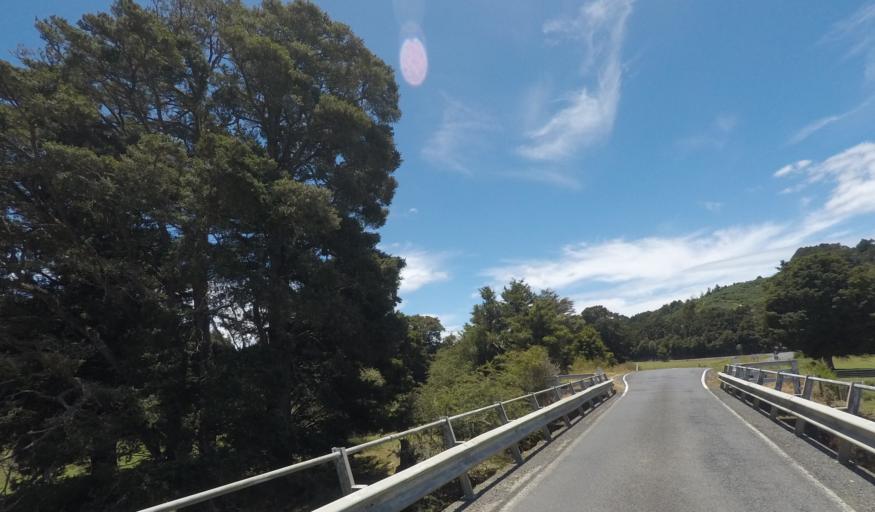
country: NZ
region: Northland
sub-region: Whangarei
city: Whangarei
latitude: -35.5421
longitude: 174.3087
